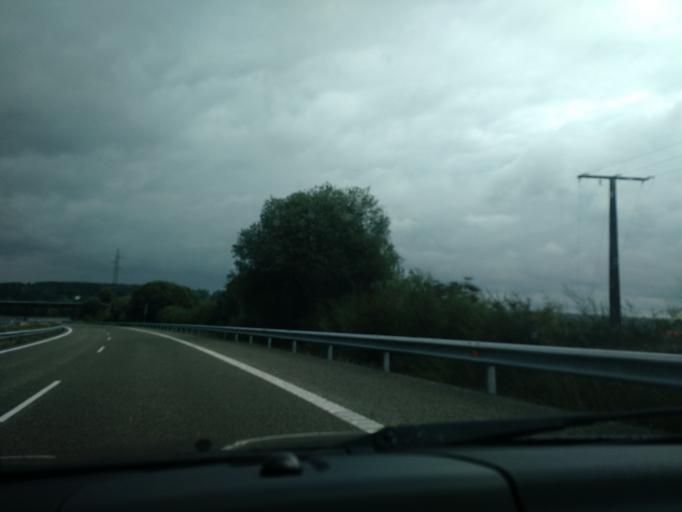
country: ES
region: Galicia
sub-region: Provincia da Coruna
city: Oroso
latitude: 42.9641
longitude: -8.4548
